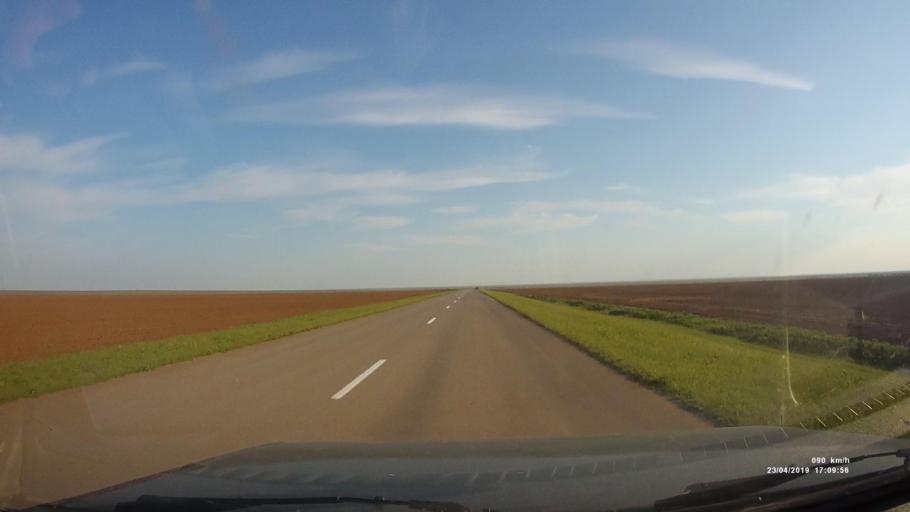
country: RU
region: Kalmykiya
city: Priyutnoye
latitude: 46.2512
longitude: 43.4842
